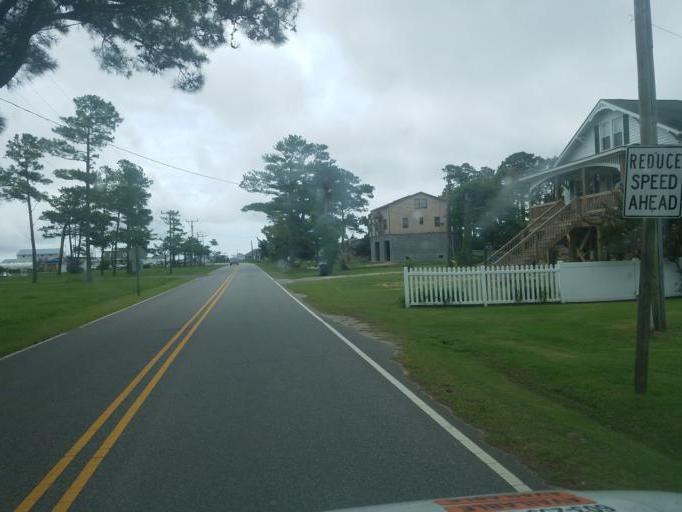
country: US
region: North Carolina
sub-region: Dare County
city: Wanchese
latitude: 35.8426
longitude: -75.6251
